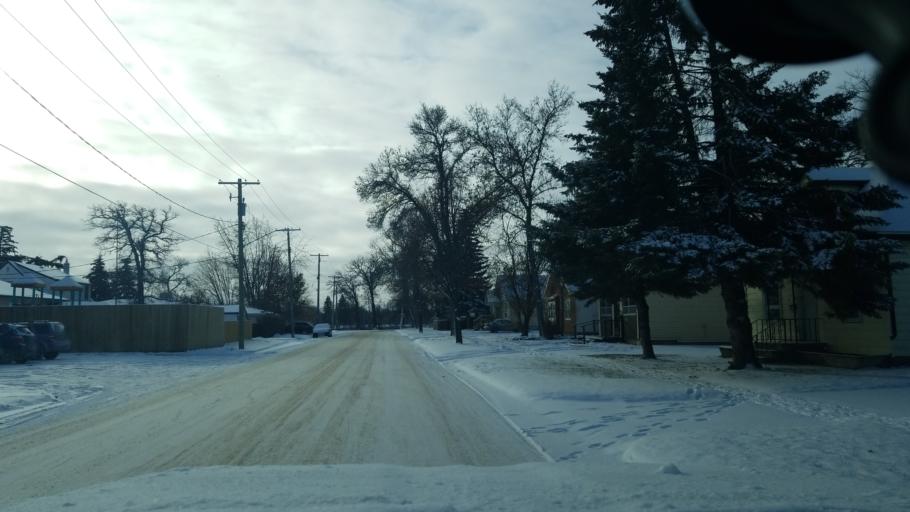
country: CA
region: Manitoba
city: Portage la Prairie
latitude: 49.9717
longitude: -98.3020
